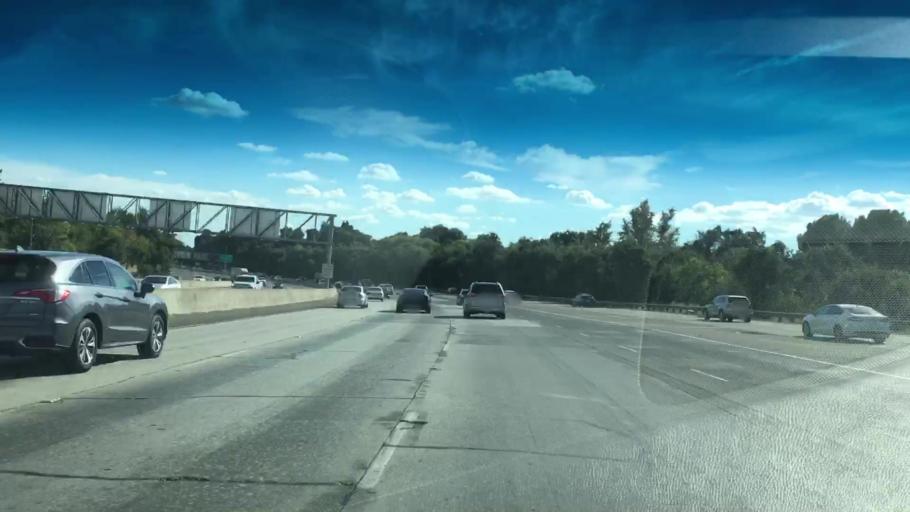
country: US
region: California
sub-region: Yolo County
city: West Sacramento
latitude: 38.5640
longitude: -121.5118
